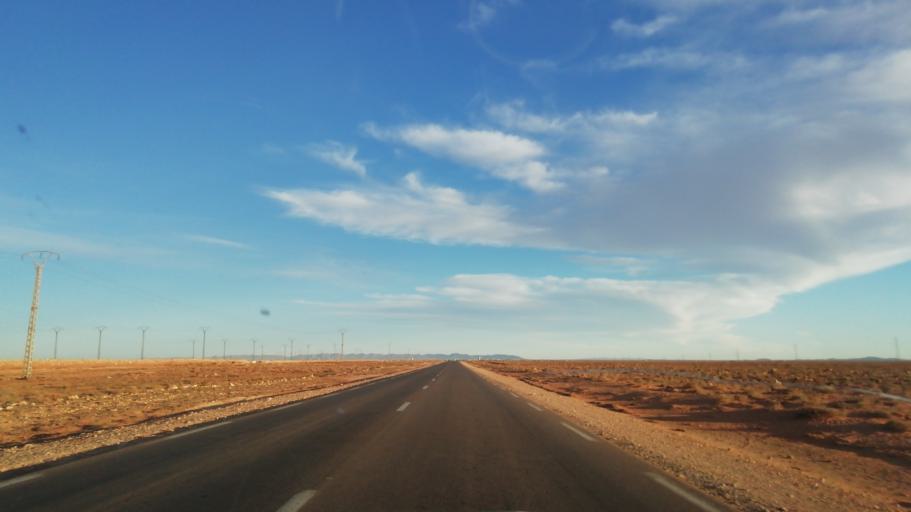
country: DZ
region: Wilaya de Naama
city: Naama
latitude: 33.7375
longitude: -0.7662
